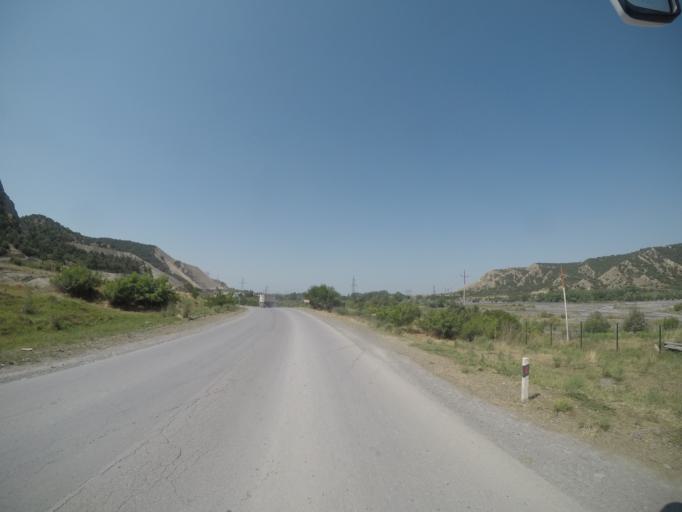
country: AZ
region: Agdas
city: Agdas
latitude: 40.7156
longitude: 47.5564
